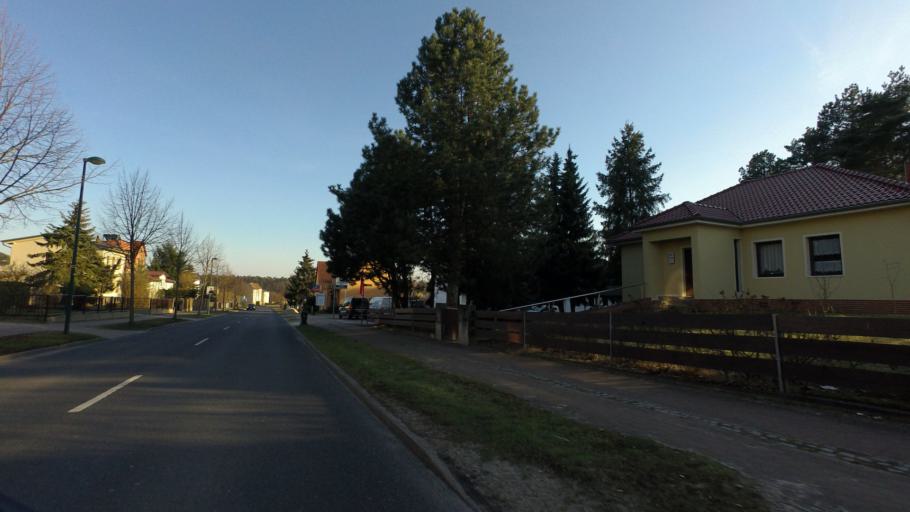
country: DE
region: Brandenburg
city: Britz
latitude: 52.8712
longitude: 13.8229
